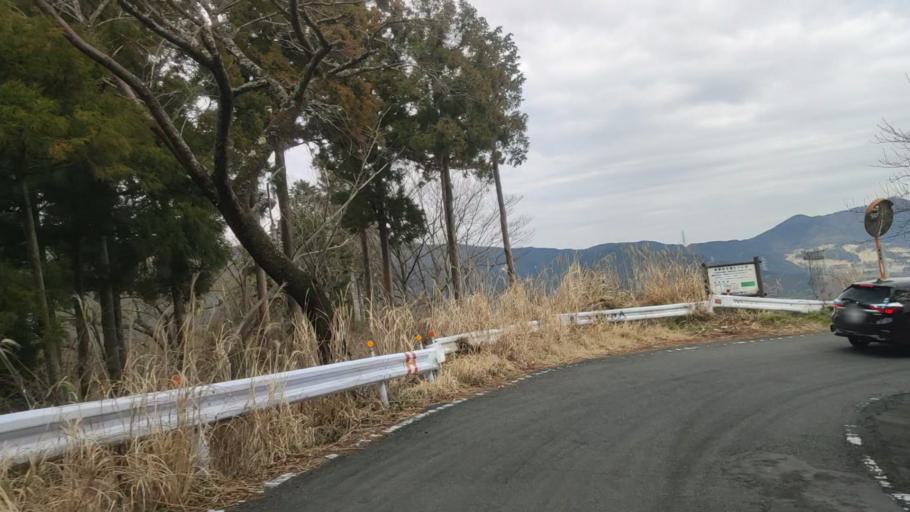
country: JP
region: Kanagawa
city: Hadano
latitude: 35.4108
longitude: 139.2153
